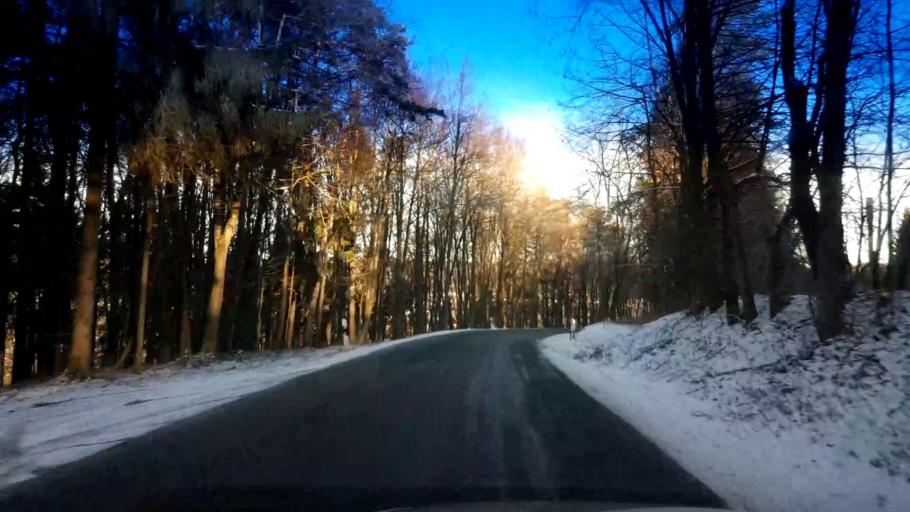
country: DE
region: Bavaria
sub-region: Upper Franconia
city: Heiligenstadt
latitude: 49.8581
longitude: 11.1541
